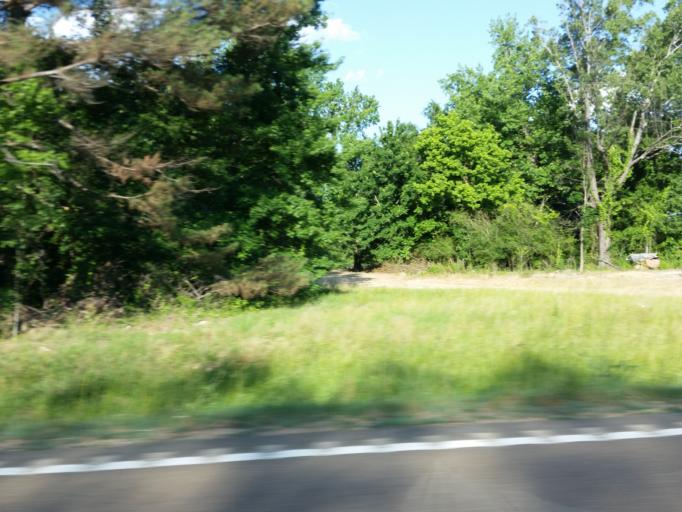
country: US
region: Mississippi
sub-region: Calhoun County
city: Calhoun City
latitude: 33.7658
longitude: -89.3638
